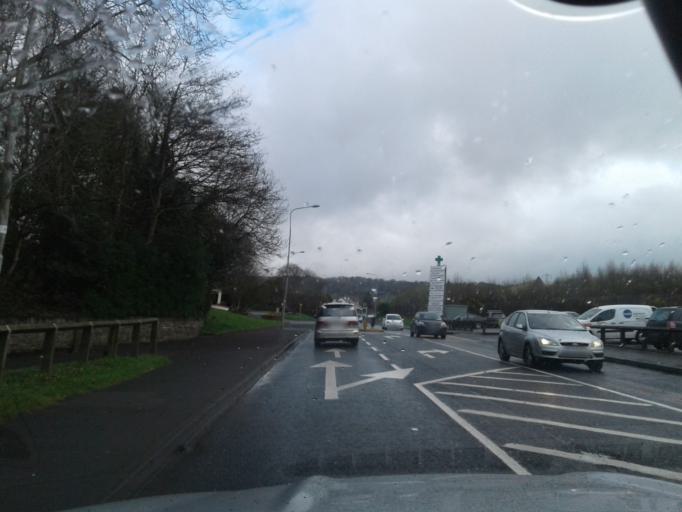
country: IE
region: Ulster
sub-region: County Donegal
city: Letterkenny
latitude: 54.9535
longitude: -7.7097
